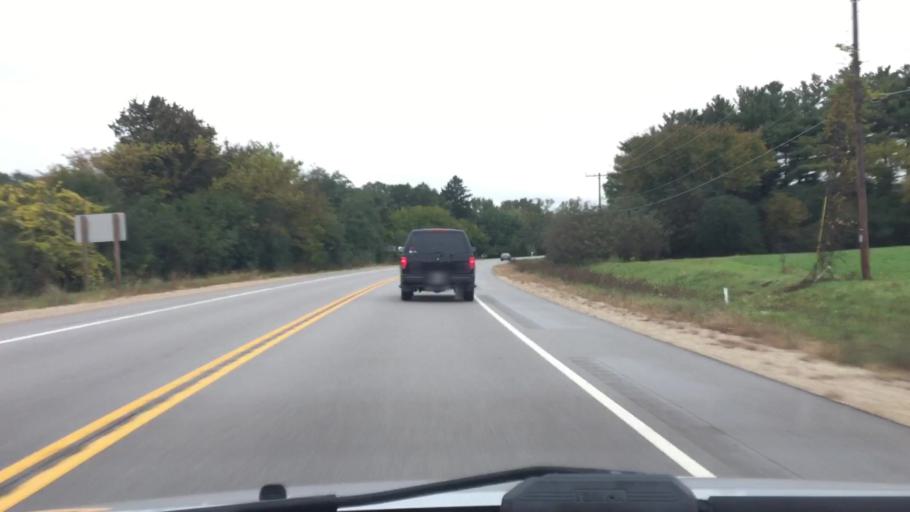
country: US
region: Wisconsin
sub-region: Waukesha County
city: Dousman
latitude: 43.0488
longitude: -88.4707
